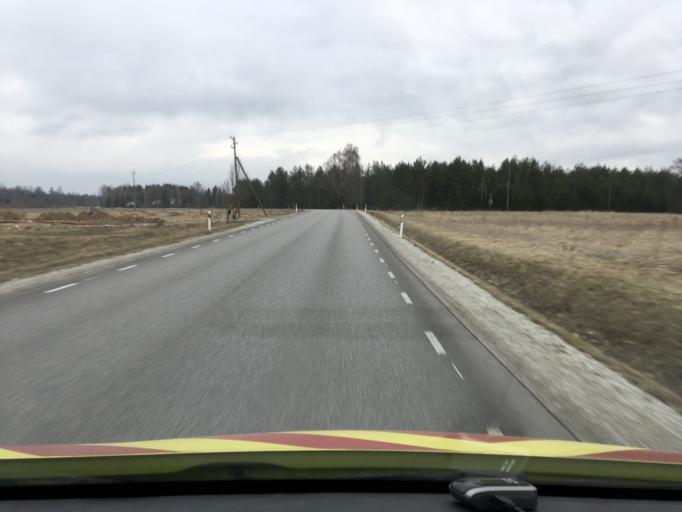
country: EE
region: Raplamaa
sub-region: Rapla vald
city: Rapla
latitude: 59.0055
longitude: 24.8425
